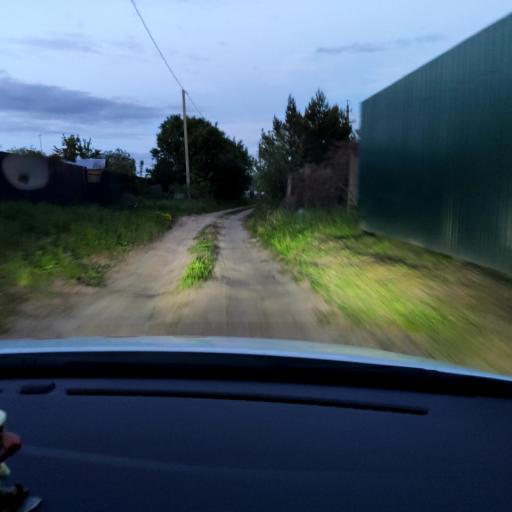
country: RU
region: Tatarstan
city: Stolbishchi
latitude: 55.5950
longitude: 49.0972
